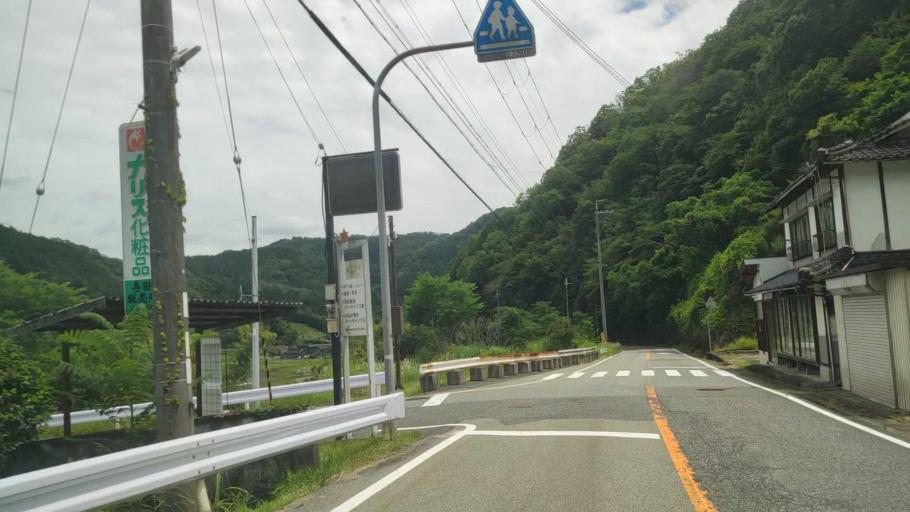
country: JP
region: Hyogo
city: Yamazakicho-nakabirose
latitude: 35.1057
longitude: 134.3599
